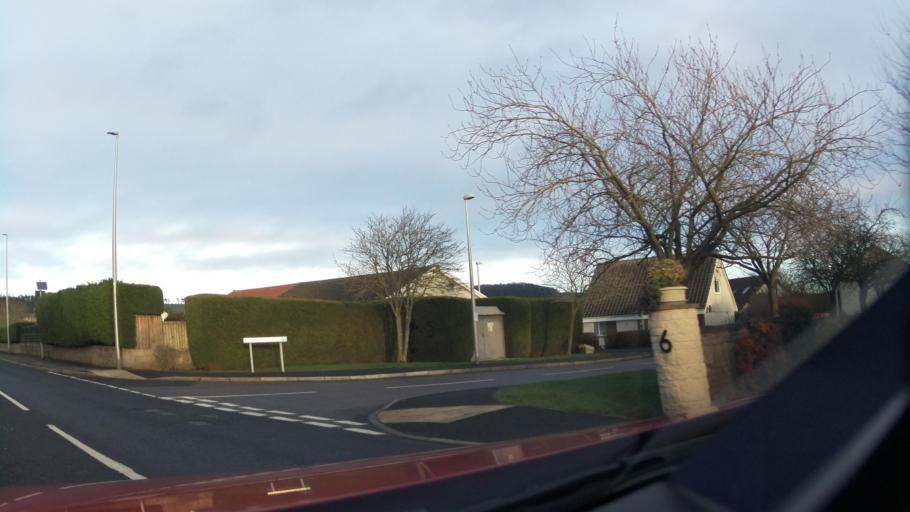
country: GB
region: Scotland
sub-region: Fife
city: Tayport
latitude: 56.5157
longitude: -2.8171
